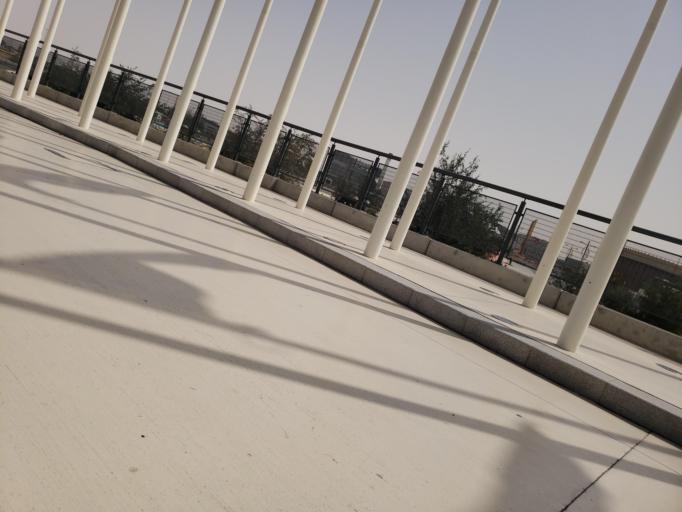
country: AE
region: Dubai
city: Dubai
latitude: 24.9678
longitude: 55.1541
